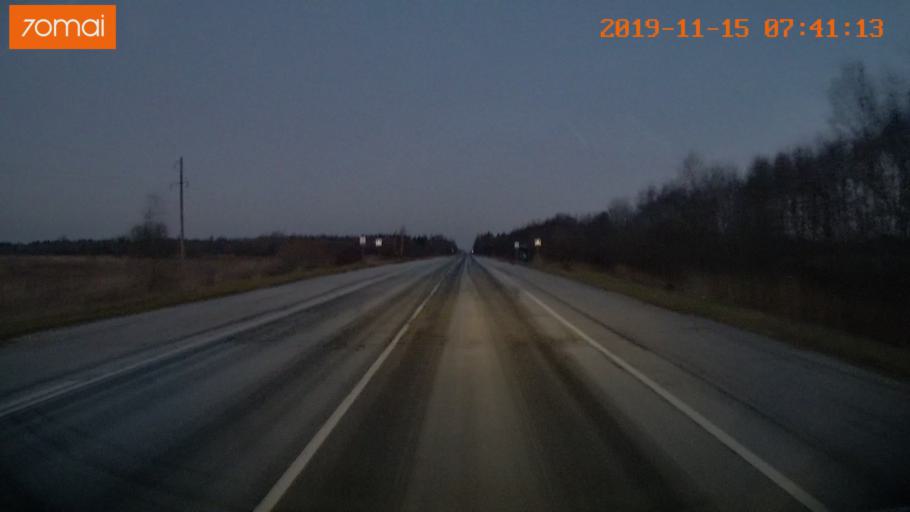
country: RU
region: Vologda
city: Sheksna
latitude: 58.7792
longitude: 38.3598
